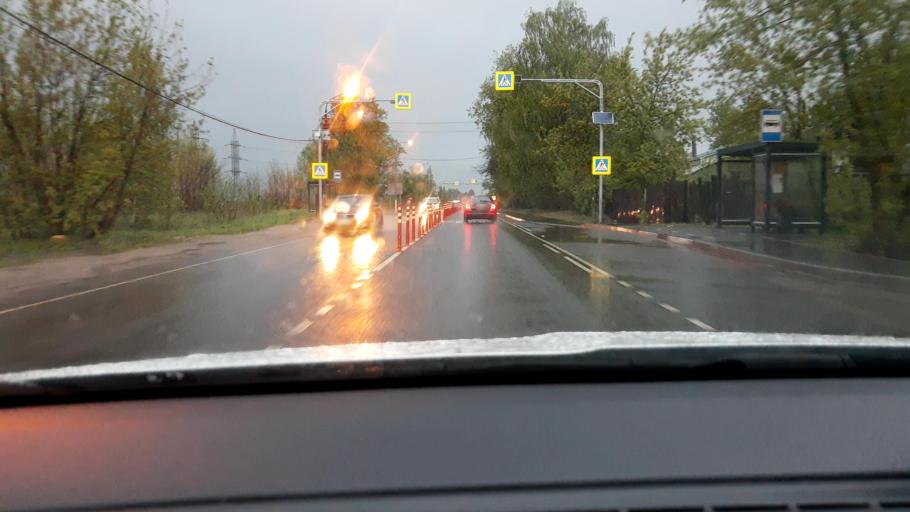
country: RU
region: Moskovskaya
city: Zagoryanskiy
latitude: 55.9286
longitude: 37.9441
